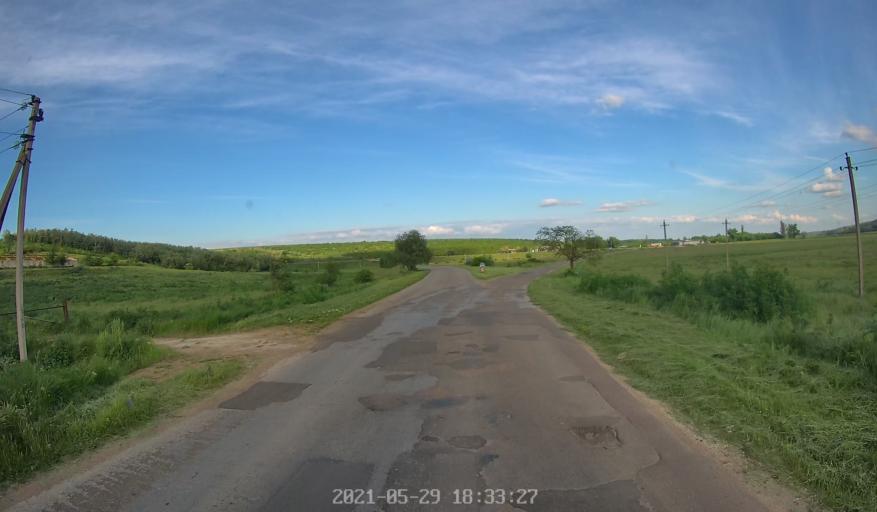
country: MD
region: Chisinau
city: Singera
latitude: 46.8160
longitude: 28.9036
